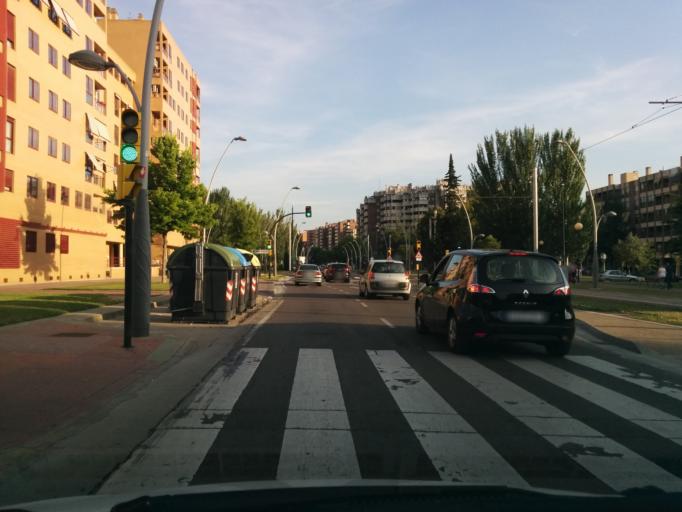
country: ES
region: Aragon
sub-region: Provincia de Zaragoza
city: Almozara
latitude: 41.6747
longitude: -0.8907
